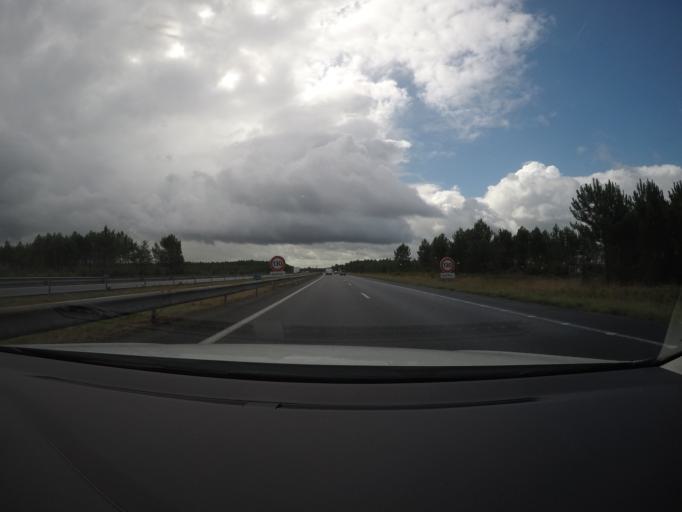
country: FR
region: Aquitaine
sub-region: Departement de la Gironde
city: Salles
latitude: 44.6184
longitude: -0.8505
